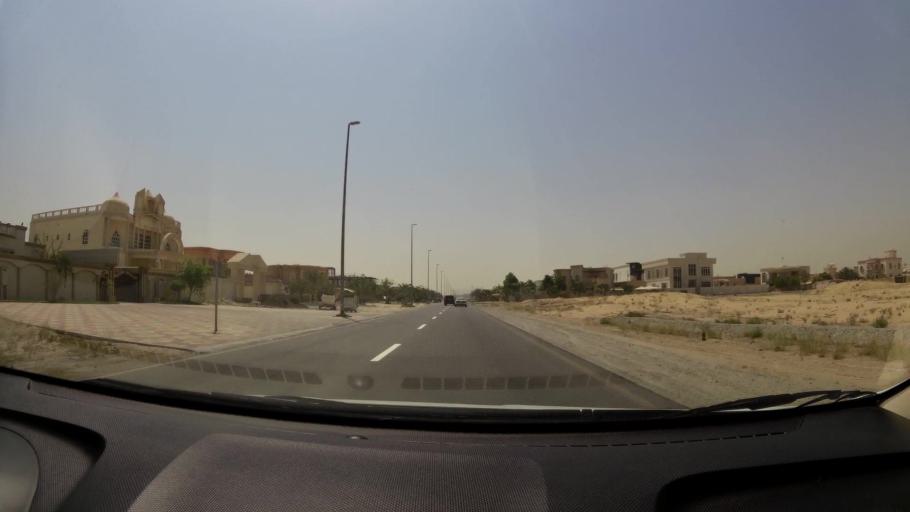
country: AE
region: Ajman
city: Ajman
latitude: 25.4173
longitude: 55.5167
